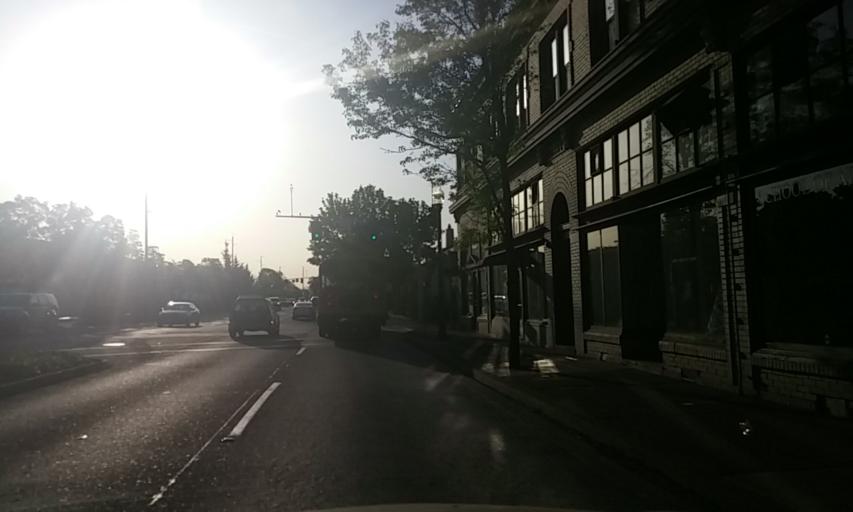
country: US
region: Oregon
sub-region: Washington County
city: Beaverton
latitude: 45.4871
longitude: -122.8065
